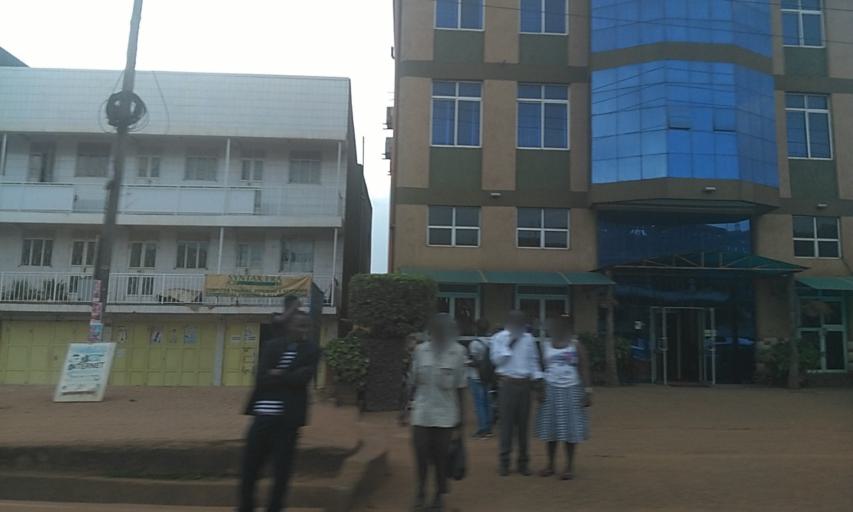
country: UG
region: Central Region
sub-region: Kampala District
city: Kampala
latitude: 0.2878
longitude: 32.5695
